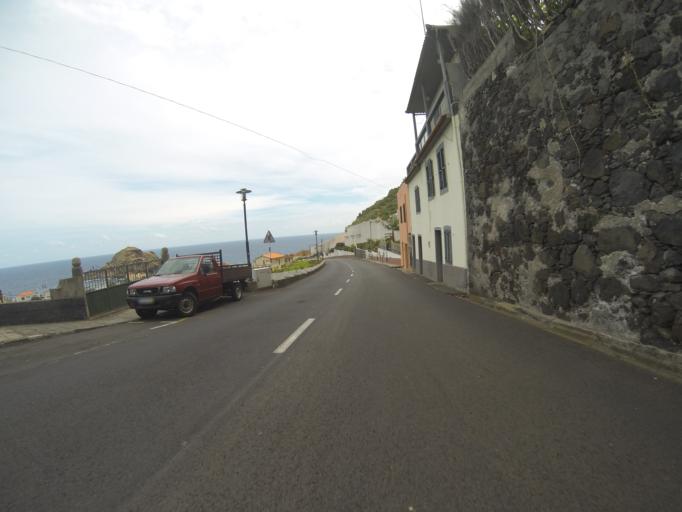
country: PT
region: Madeira
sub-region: Porto Moniz
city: Porto Moniz
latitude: 32.8646
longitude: -17.1663
